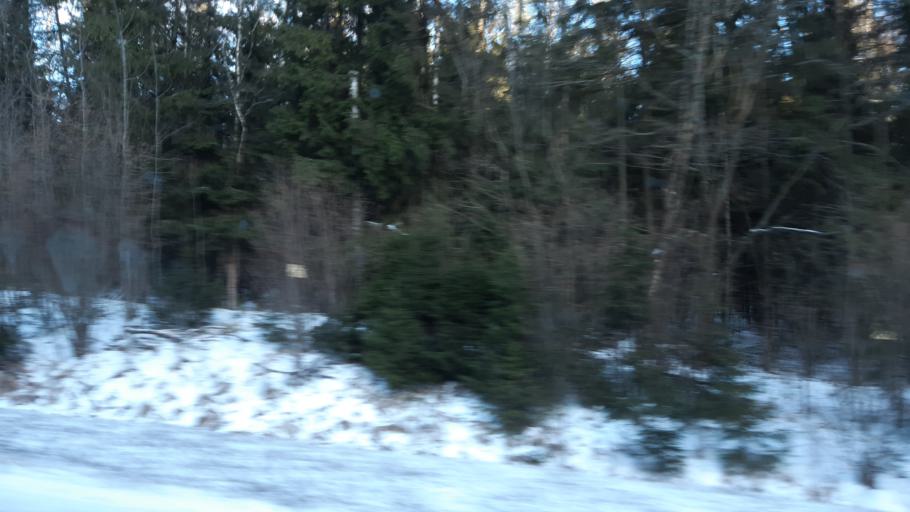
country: RU
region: Vladimir
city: Arsaki
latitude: 56.2764
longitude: 38.4092
